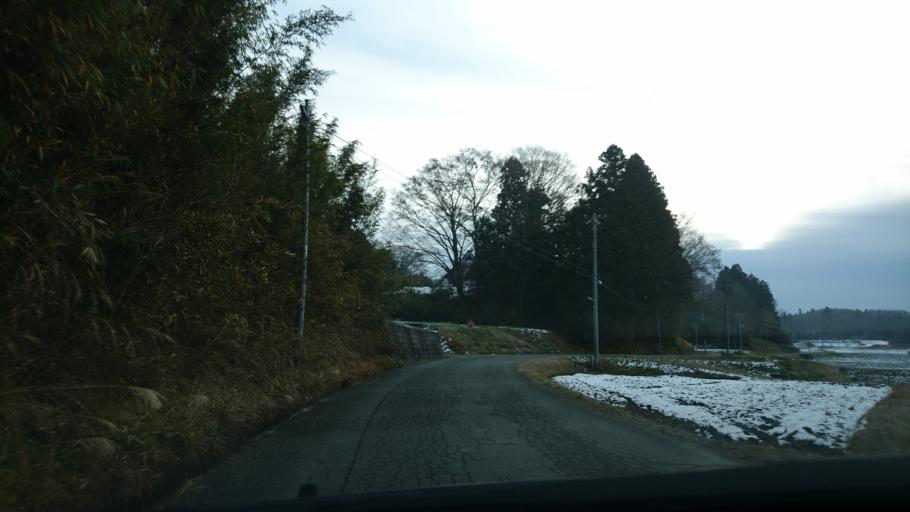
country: JP
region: Iwate
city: Ichinoseki
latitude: 38.9066
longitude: 141.3432
